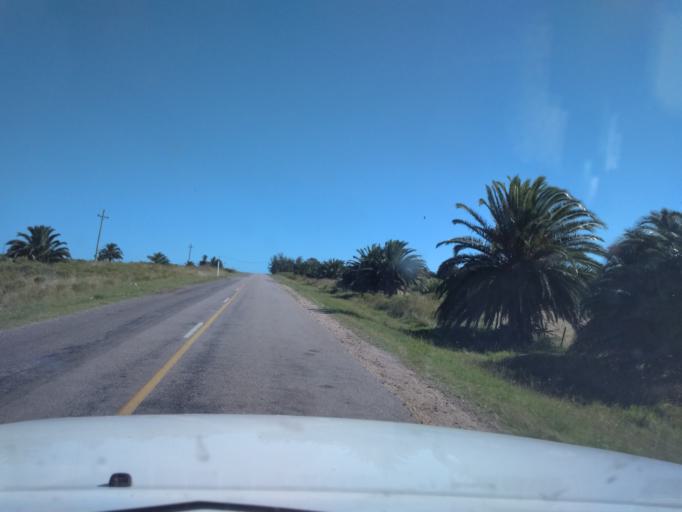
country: UY
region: Canelones
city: San Ramon
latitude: -34.1605
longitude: -55.9470
